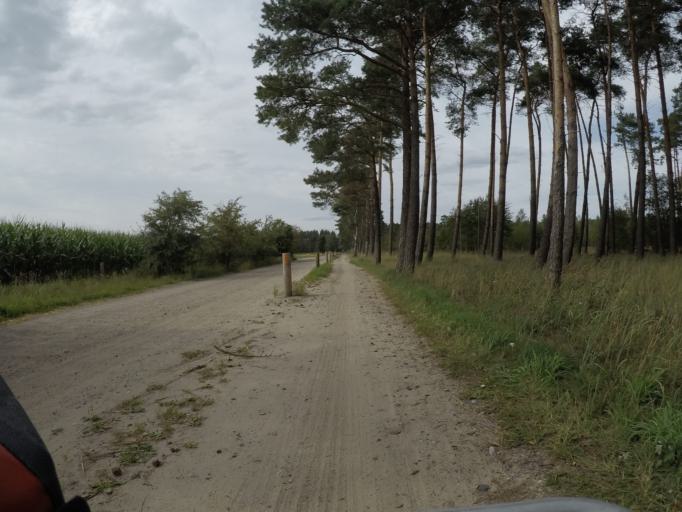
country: DE
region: Lower Saxony
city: Bardowick
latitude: 53.3123
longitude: 10.4015
